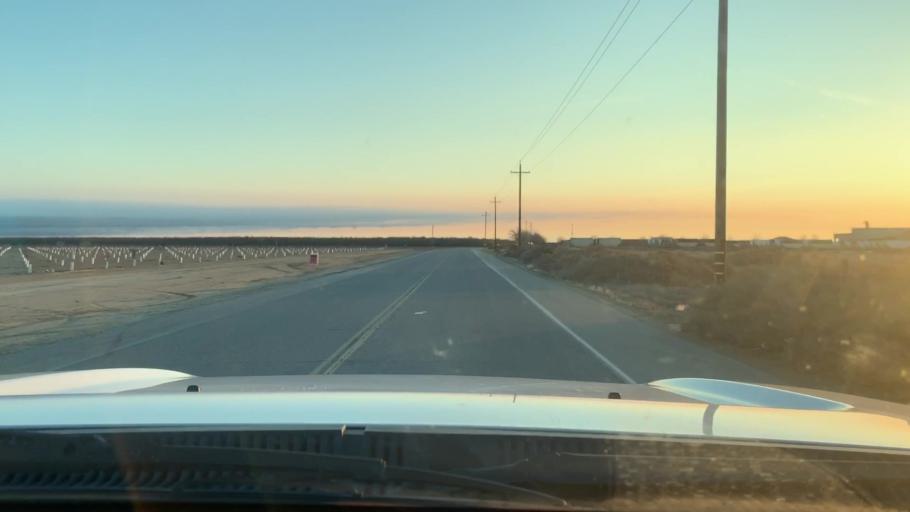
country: US
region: California
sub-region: Kern County
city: Buttonwillow
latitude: 35.5007
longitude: -119.5316
